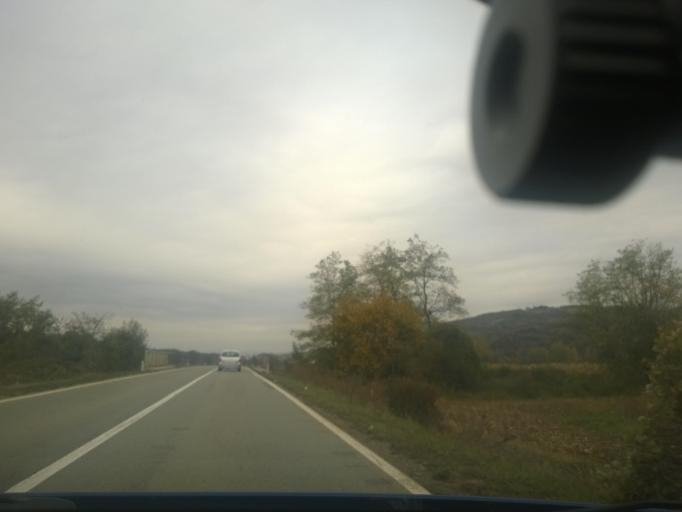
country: RS
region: Central Serbia
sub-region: Pirotski Okrug
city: Dimitrovgrad
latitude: 43.0390
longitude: 22.7094
